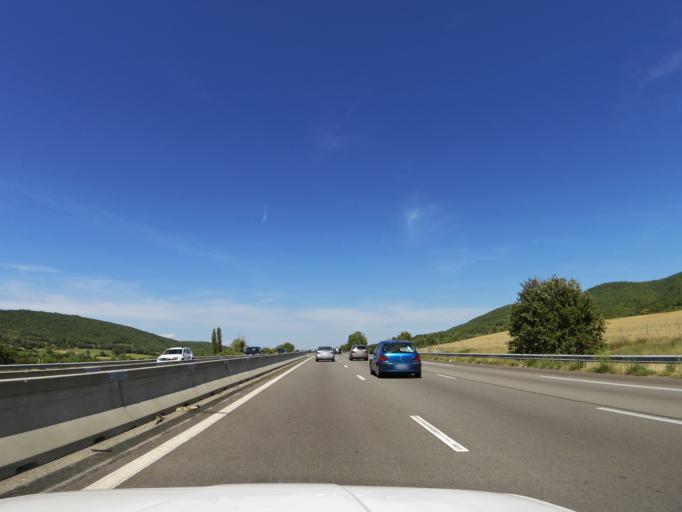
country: FR
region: Rhone-Alpes
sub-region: Departement de la Drome
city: Savasse
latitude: 44.6157
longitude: 4.7928
